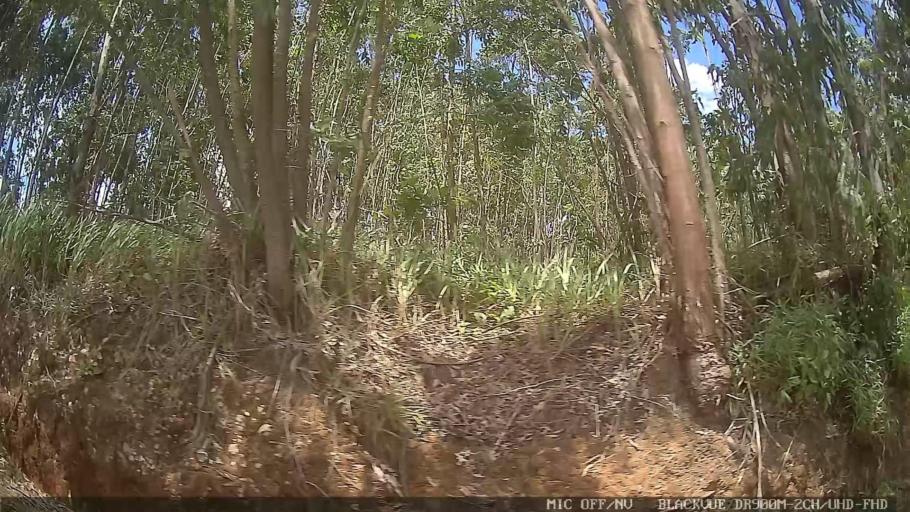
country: BR
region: Minas Gerais
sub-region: Extrema
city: Extrema
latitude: -22.7468
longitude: -46.4330
